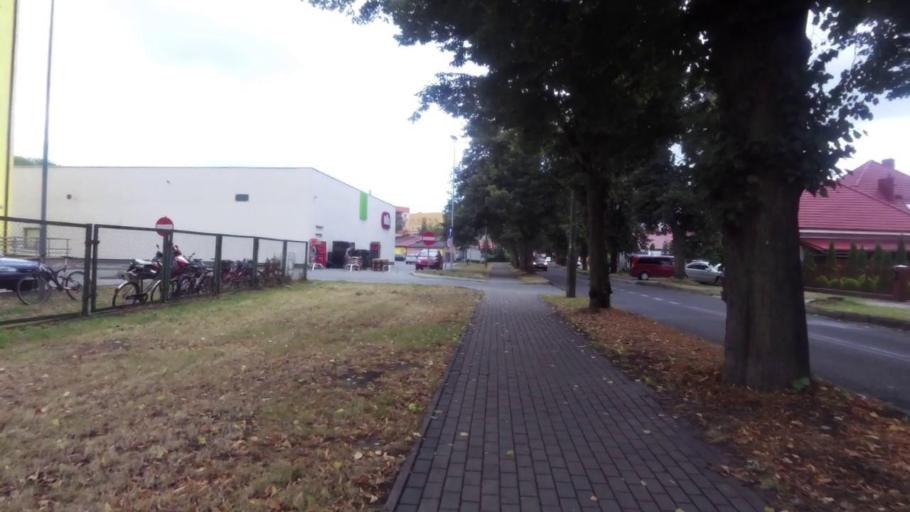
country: PL
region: Lubusz
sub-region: Powiat gorzowski
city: Kostrzyn nad Odra
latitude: 52.5985
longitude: 14.6366
